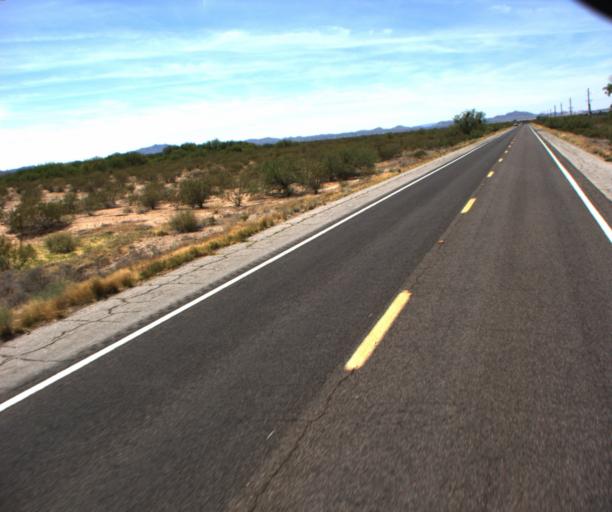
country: US
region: Arizona
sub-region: La Paz County
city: Salome
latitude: 33.8290
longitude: -113.5120
